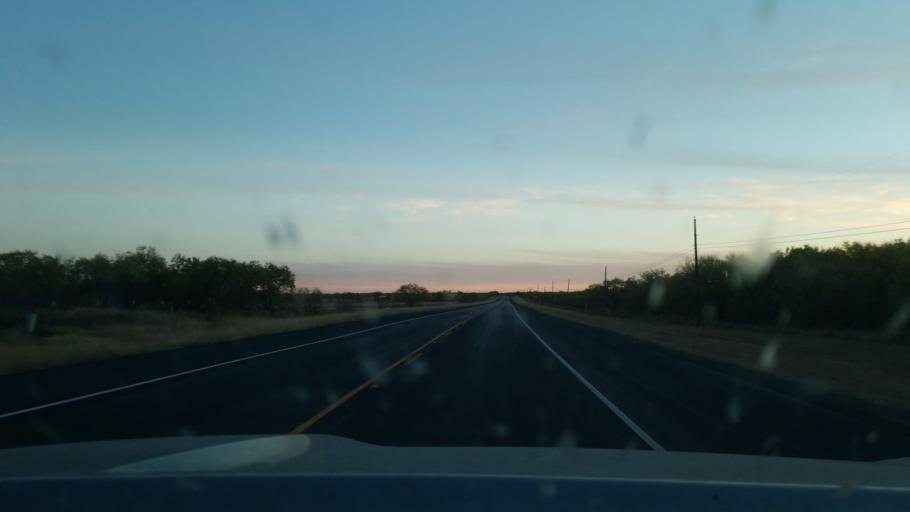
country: US
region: Texas
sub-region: Stephens County
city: Breckenridge
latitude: 32.6398
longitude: -98.9027
